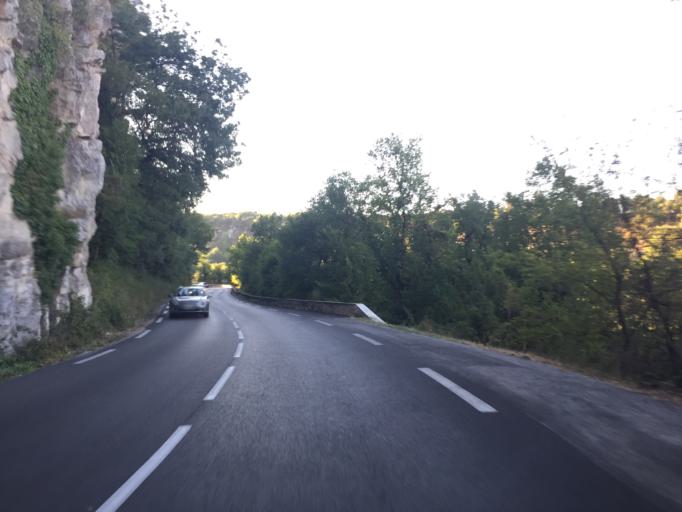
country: FR
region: Provence-Alpes-Cote d'Azur
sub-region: Departement des Alpes-de-Haute-Provence
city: Cereste
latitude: 43.8586
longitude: 5.5861
